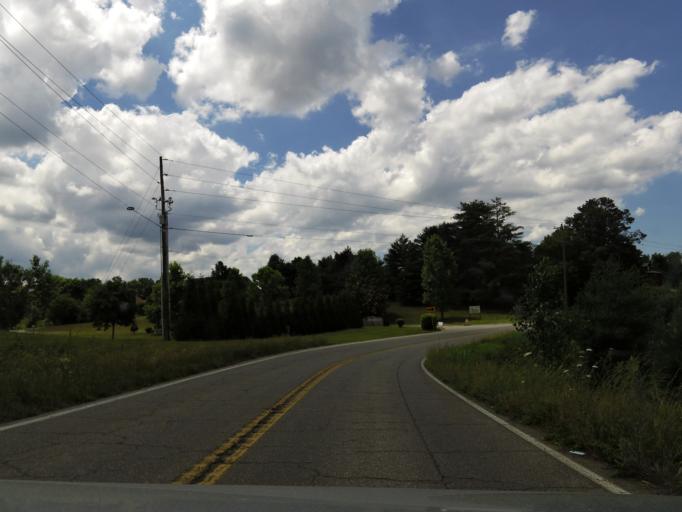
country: US
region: Tennessee
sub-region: Loudon County
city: Greenback
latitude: 35.6272
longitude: -84.0830
